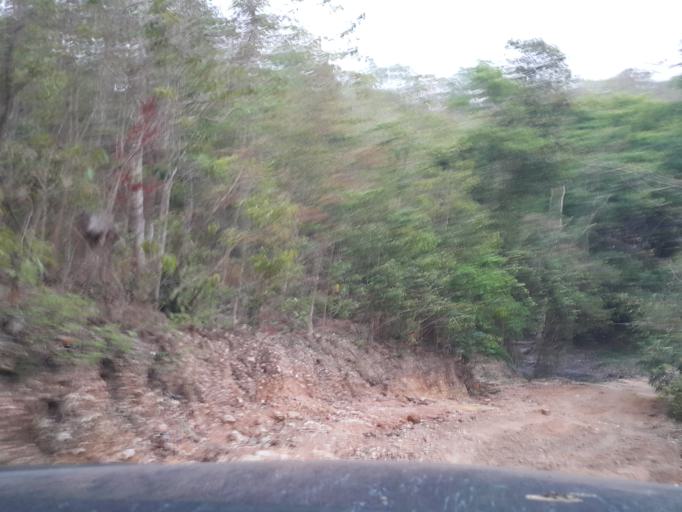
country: TH
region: Lamphun
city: Thung Hua Chang
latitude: 17.8965
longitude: 99.0844
